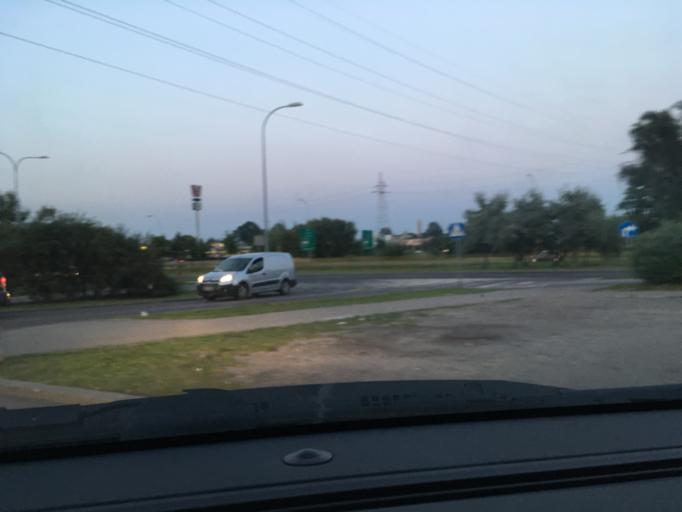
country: PL
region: Podlasie
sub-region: Bialystok
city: Bialystok
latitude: 53.1241
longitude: 23.1804
